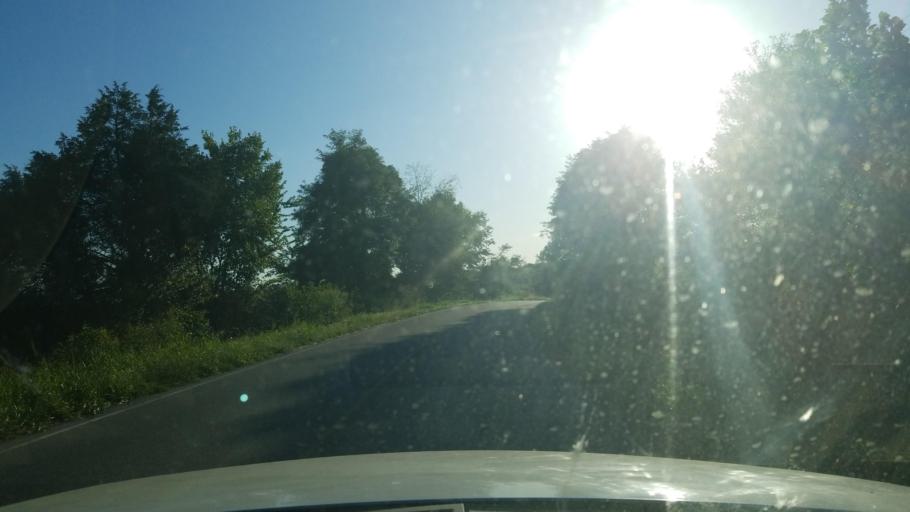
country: US
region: Illinois
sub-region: Hardin County
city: Elizabethtown
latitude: 37.5742
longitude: -88.3903
